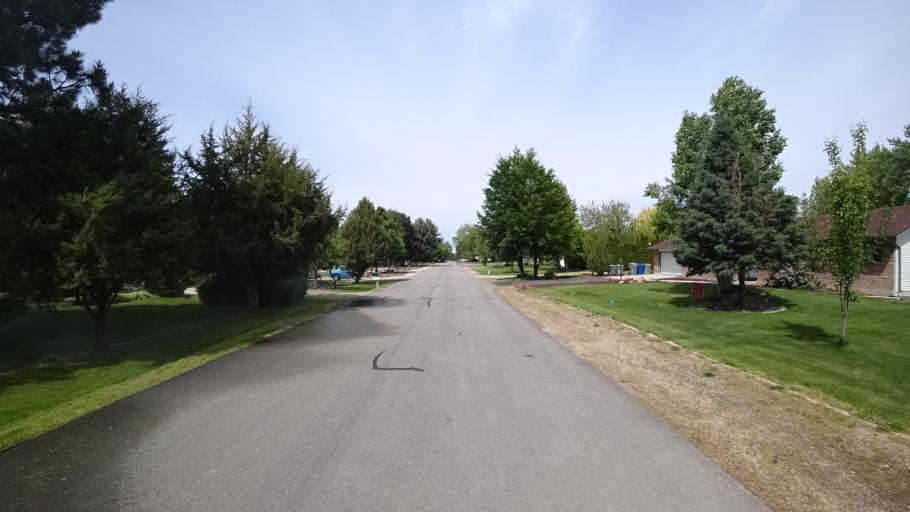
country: US
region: Idaho
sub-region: Ada County
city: Meridian
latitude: 43.5801
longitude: -116.3178
